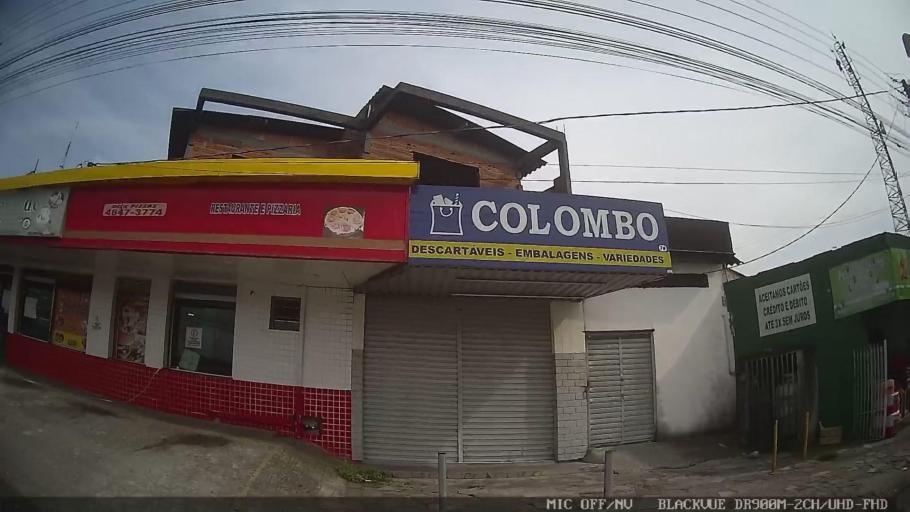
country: BR
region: Sao Paulo
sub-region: Itaquaquecetuba
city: Itaquaquecetuba
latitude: -23.4964
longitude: -46.3577
